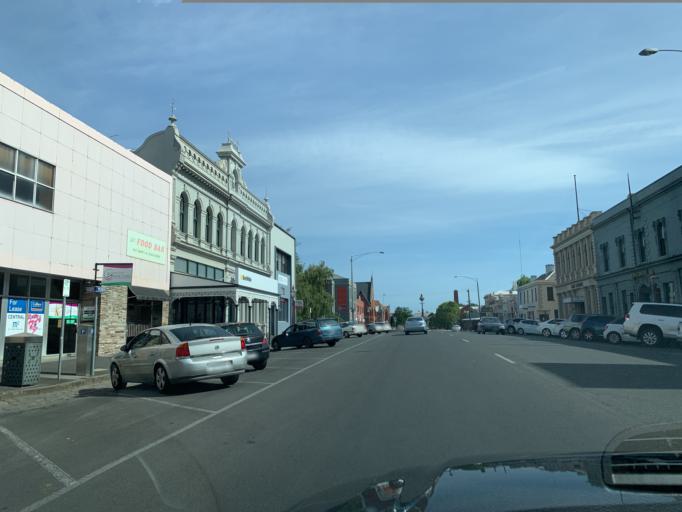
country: AU
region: Victoria
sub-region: Ballarat North
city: Ballarat Central
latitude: -37.5628
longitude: 143.8576
